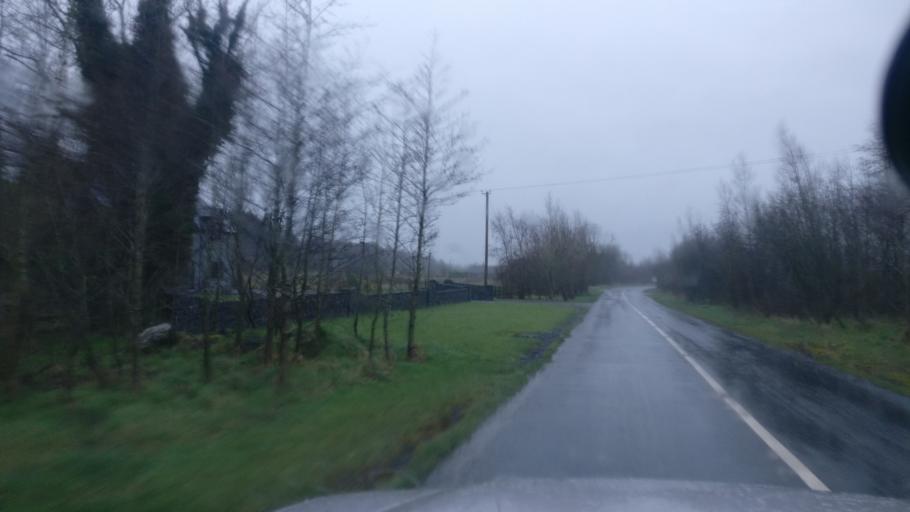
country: IE
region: Connaught
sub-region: County Galway
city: Ballinasloe
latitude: 53.3071
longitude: -8.3373
